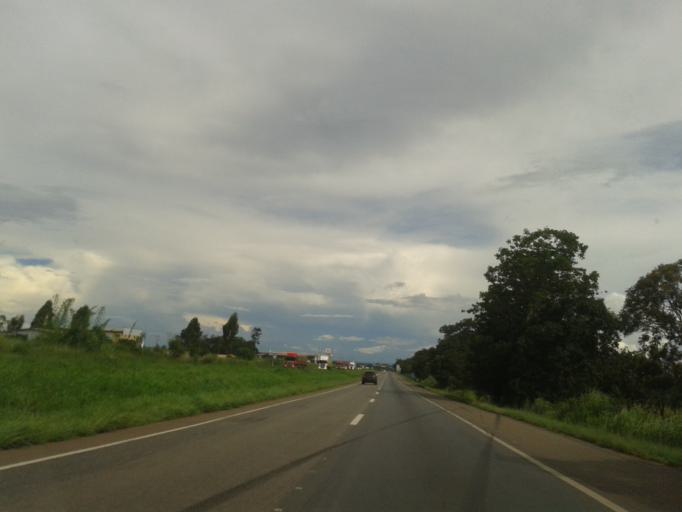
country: BR
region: Goias
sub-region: Hidrolandia
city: Hidrolandia
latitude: -16.9446
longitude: -49.2520
